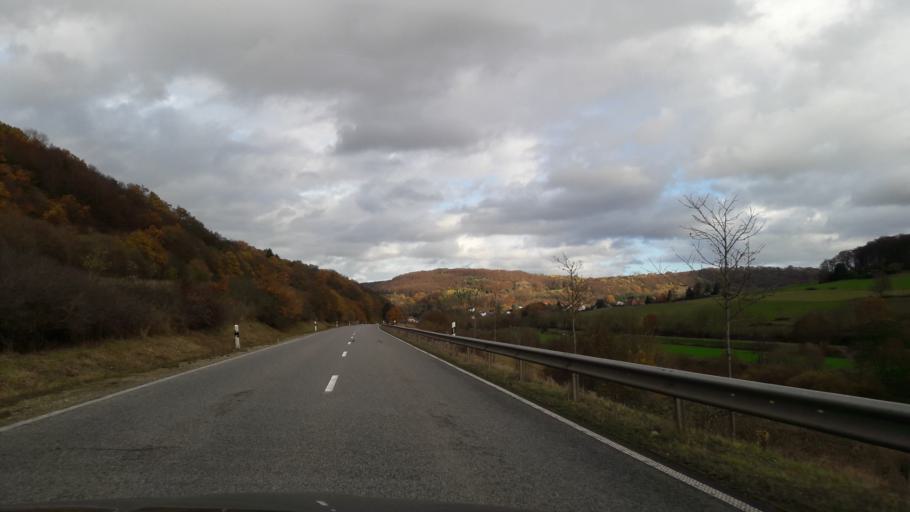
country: DE
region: Rheinland-Pfalz
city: Minden
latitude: 49.8153
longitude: 6.4571
